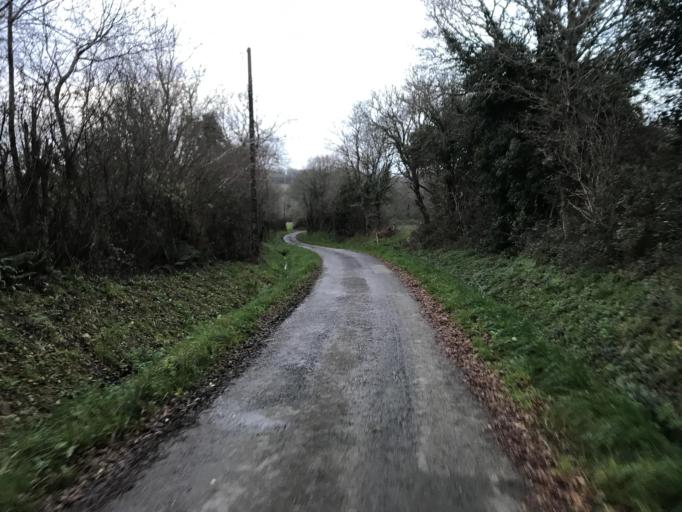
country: FR
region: Brittany
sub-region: Departement du Finistere
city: Loperhet
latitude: 48.3604
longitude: -4.3151
